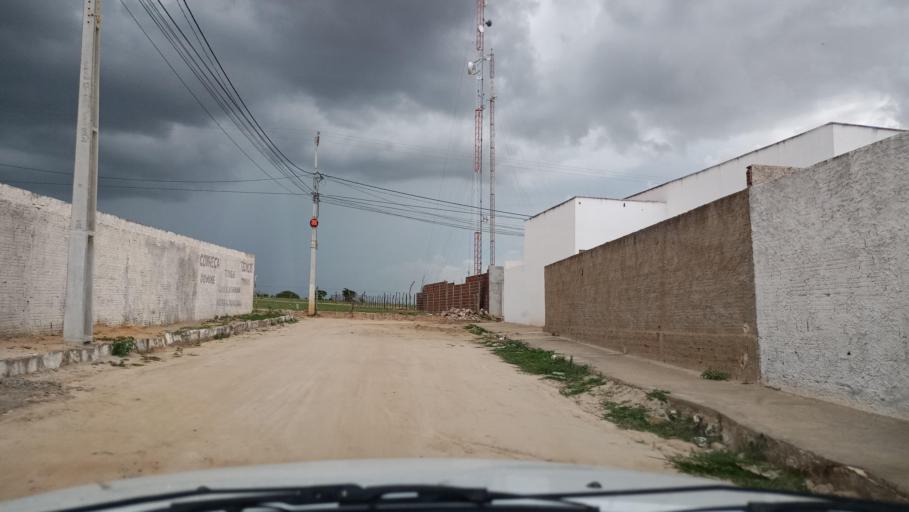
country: BR
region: Rio Grande do Norte
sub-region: Tangara
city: Tangara
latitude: -6.0970
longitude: -35.7148
